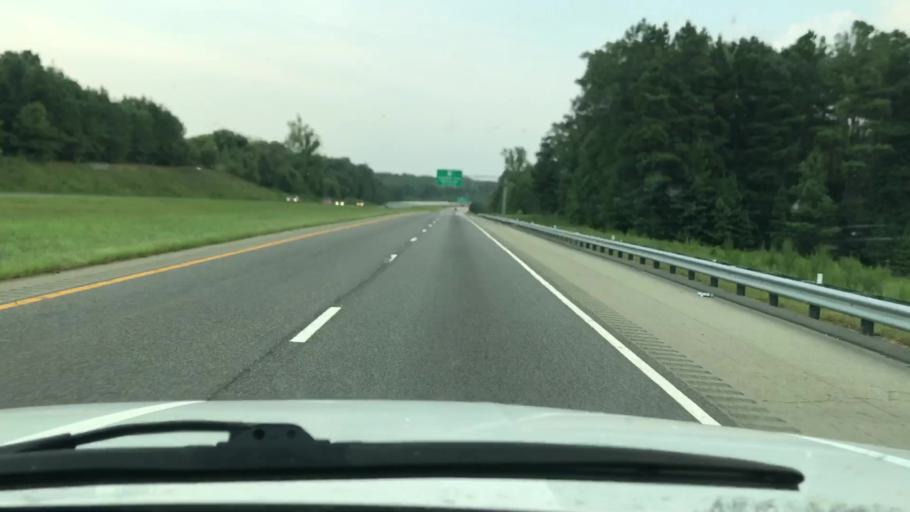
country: US
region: Virginia
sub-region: Chesterfield County
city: Brandermill
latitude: 37.5463
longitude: -77.6939
